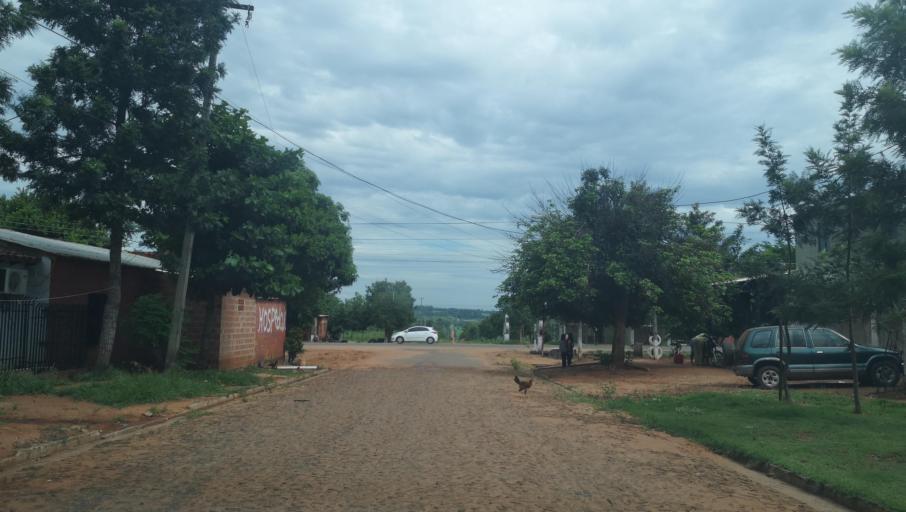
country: PY
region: San Pedro
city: Capiibary
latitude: -24.7196
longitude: -56.0143
